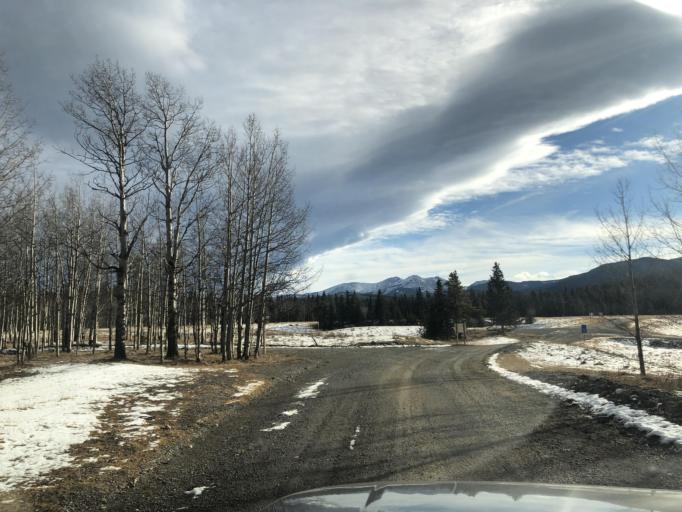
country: CA
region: Alberta
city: Cochrane
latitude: 51.0469
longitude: -114.8666
